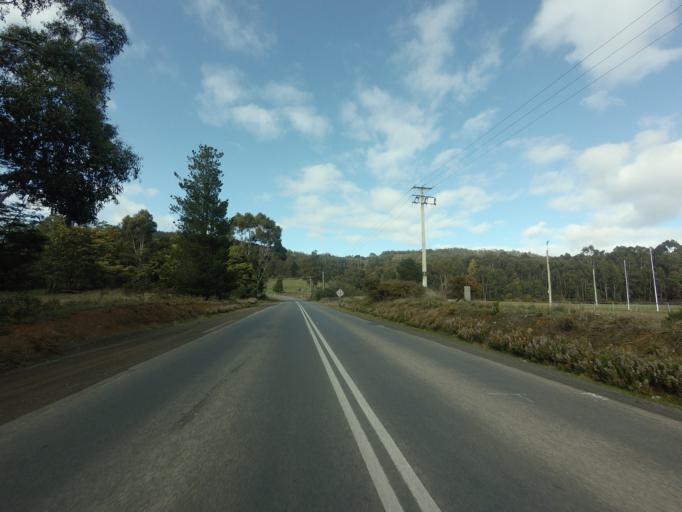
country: AU
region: Tasmania
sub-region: Huon Valley
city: Geeveston
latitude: -43.1669
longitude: 146.9410
